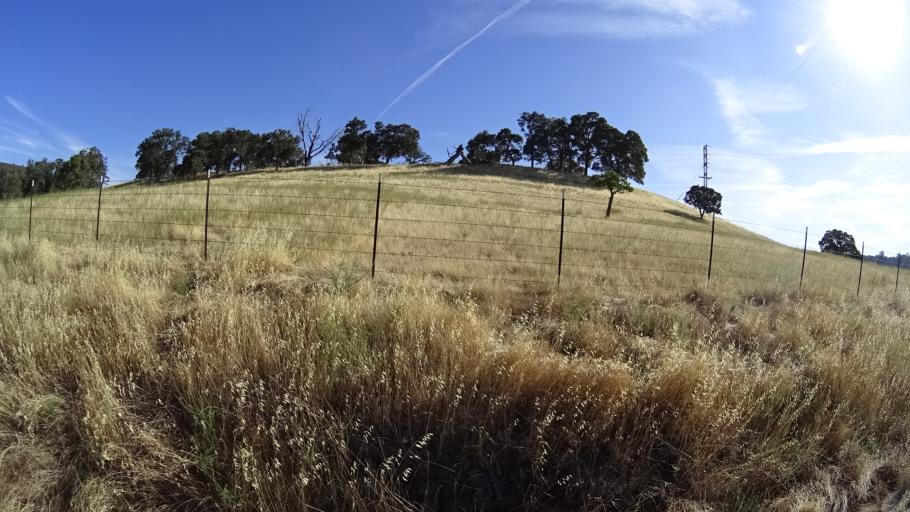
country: US
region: California
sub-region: Calaveras County
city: Valley Springs
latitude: 38.2316
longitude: -120.7965
